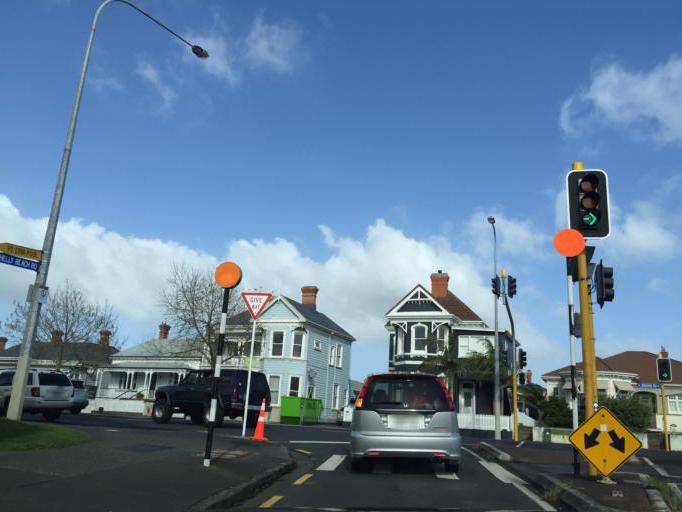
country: NZ
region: Auckland
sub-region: Auckland
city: Auckland
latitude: -36.8454
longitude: 174.7413
